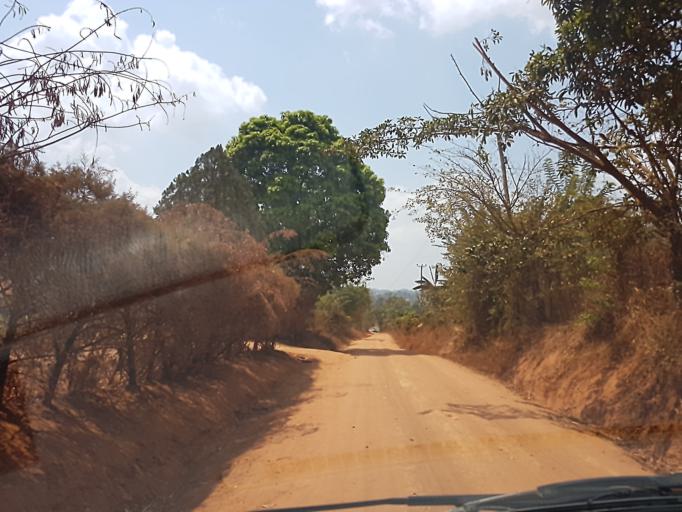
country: UG
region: Central Region
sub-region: Wakiso District
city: Bweyogerere
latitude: 0.4755
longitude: 32.6360
